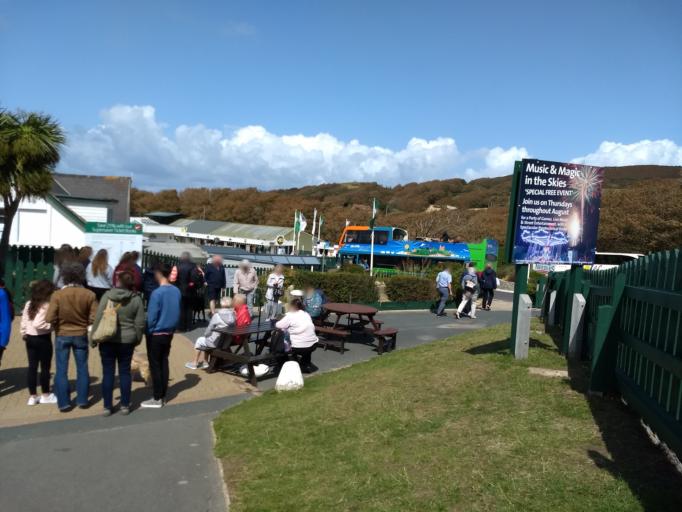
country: GB
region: England
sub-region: Isle of Wight
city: Totland
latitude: 50.6675
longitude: -1.5658
